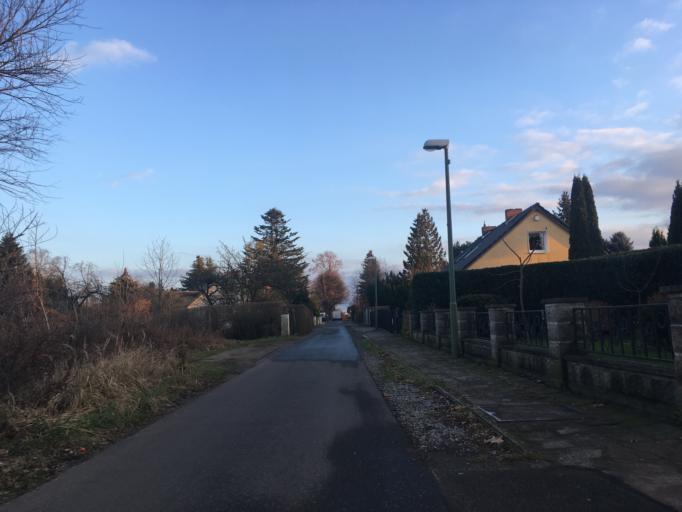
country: DE
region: Berlin
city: Buch
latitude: 52.6180
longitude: 13.4989
